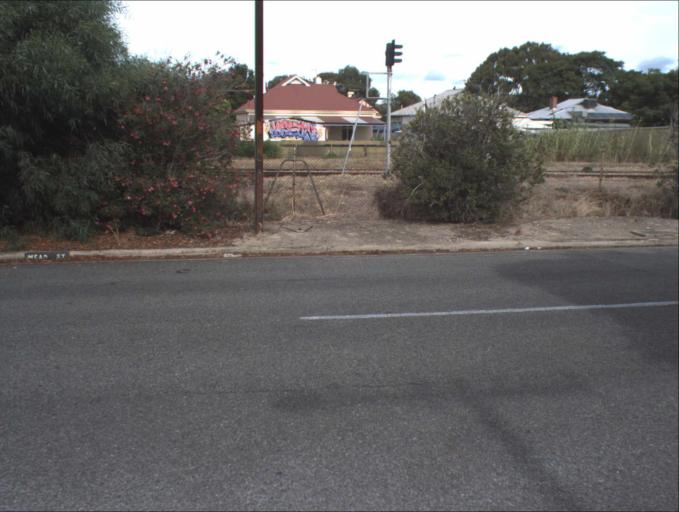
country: AU
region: South Australia
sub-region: Port Adelaide Enfield
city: Birkenhead
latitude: -34.8297
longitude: 138.4918
